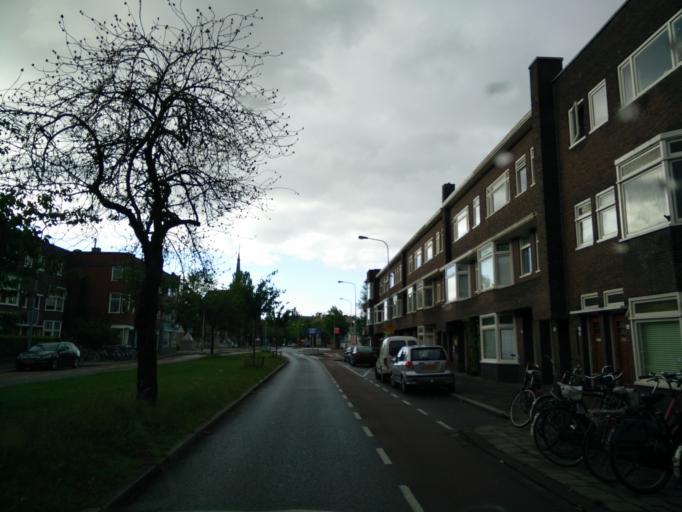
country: NL
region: Groningen
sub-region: Gemeente Groningen
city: Korrewegwijk
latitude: 53.2280
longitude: 6.5697
